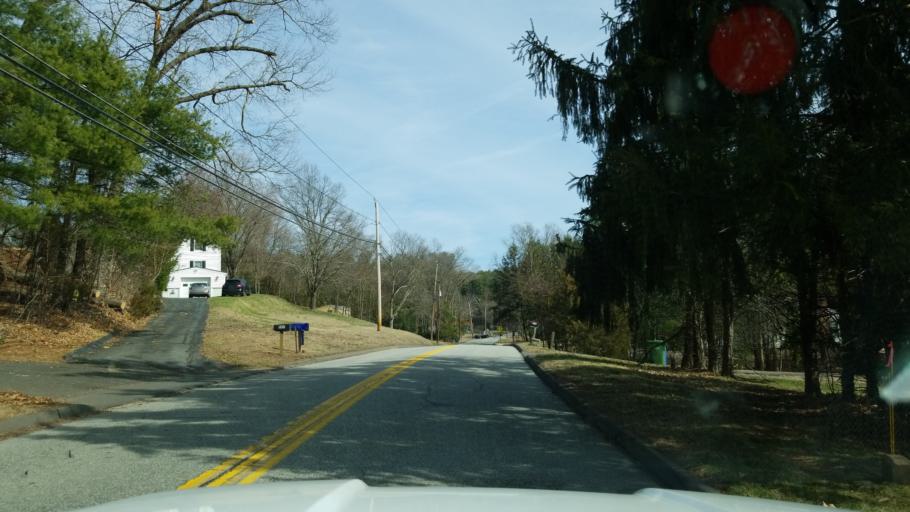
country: US
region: Connecticut
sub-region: Hartford County
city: Glastonbury Center
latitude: 41.7040
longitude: -72.5638
